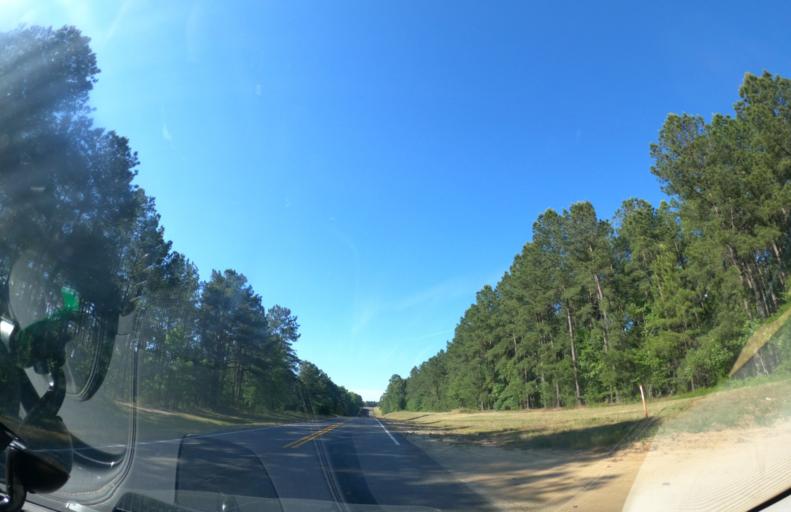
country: US
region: Georgia
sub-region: Columbia County
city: Harlem
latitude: 33.3632
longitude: -82.3247
